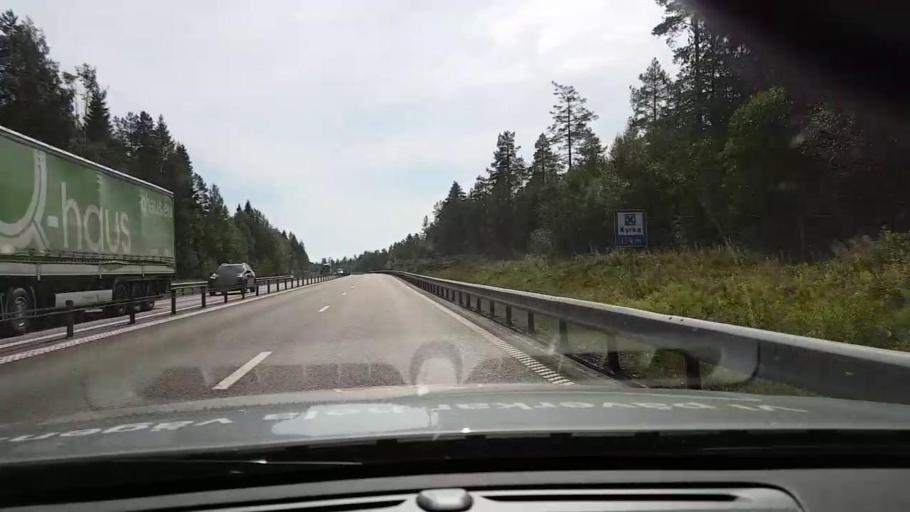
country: SE
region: Vaesternorrland
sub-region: OErnskoeldsviks Kommun
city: Husum
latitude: 63.3831
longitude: 19.1926
